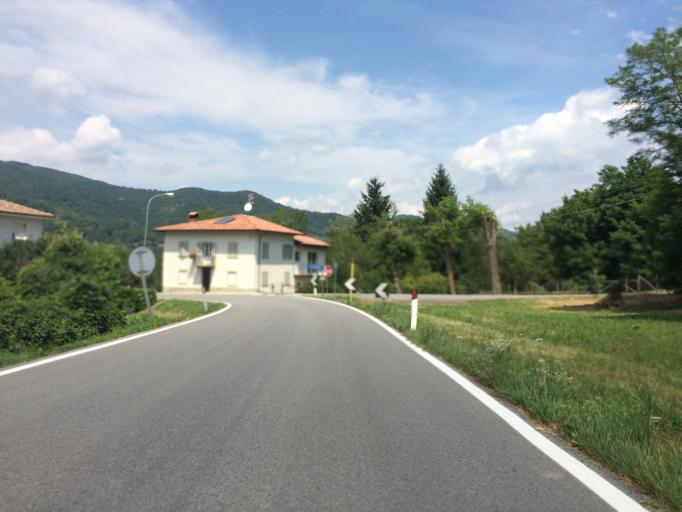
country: IT
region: Piedmont
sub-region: Provincia di Cuneo
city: Bagnasco
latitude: 44.3071
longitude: 8.0551
